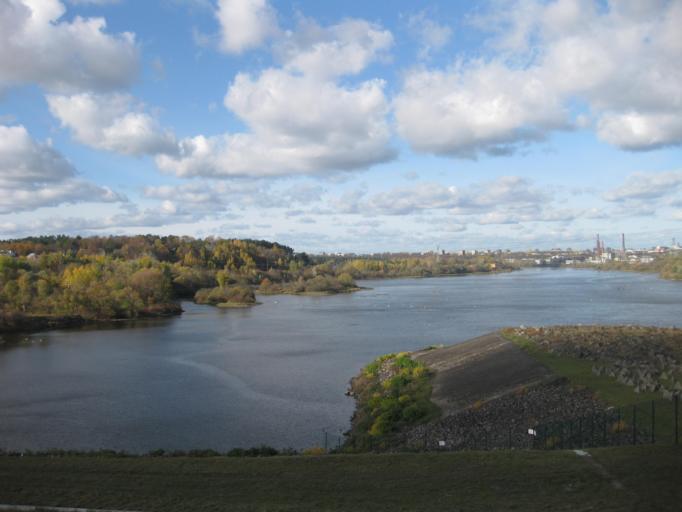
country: LT
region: Kauno apskritis
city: Dainava (Kaunas)
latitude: 54.8744
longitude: 23.9998
